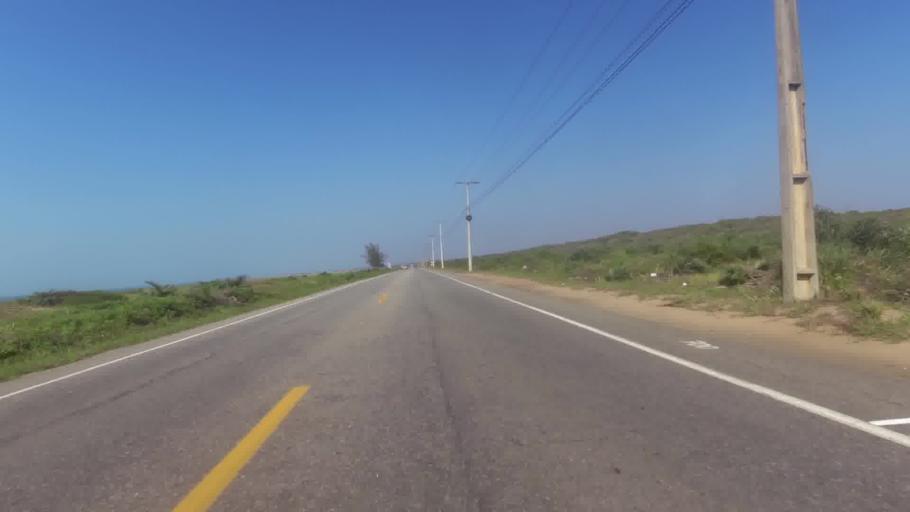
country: BR
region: Espirito Santo
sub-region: Itapemirim
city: Itapemirim
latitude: -20.9471
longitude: -40.8060
